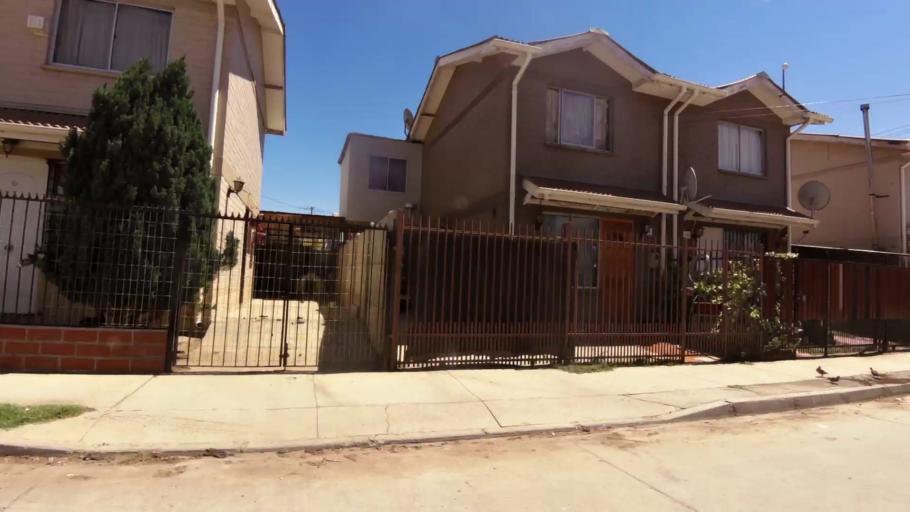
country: CL
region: O'Higgins
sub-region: Provincia de Cachapoal
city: Rancagua
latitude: -34.1531
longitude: -70.7103
